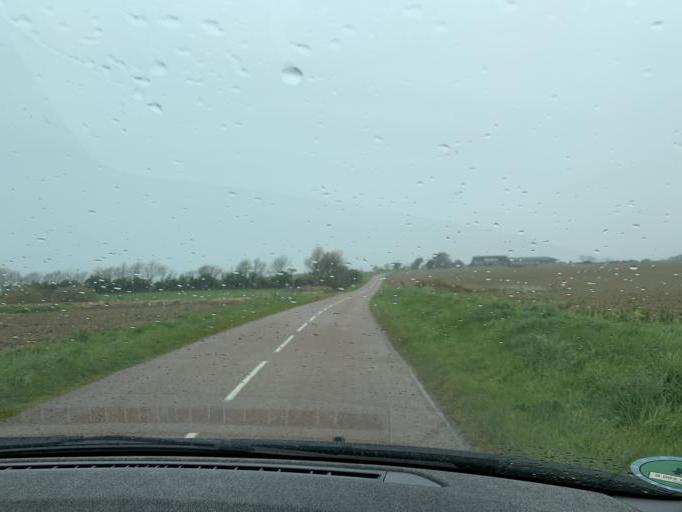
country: FR
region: Haute-Normandie
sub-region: Departement de la Seine-Maritime
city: Yport
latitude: 49.7357
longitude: 0.2982
